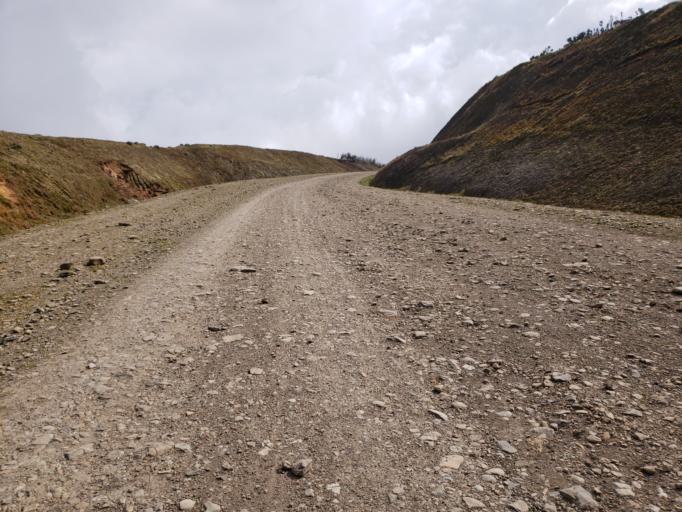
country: ET
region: Oromiya
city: Dodola
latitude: 6.7515
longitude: 39.4285
